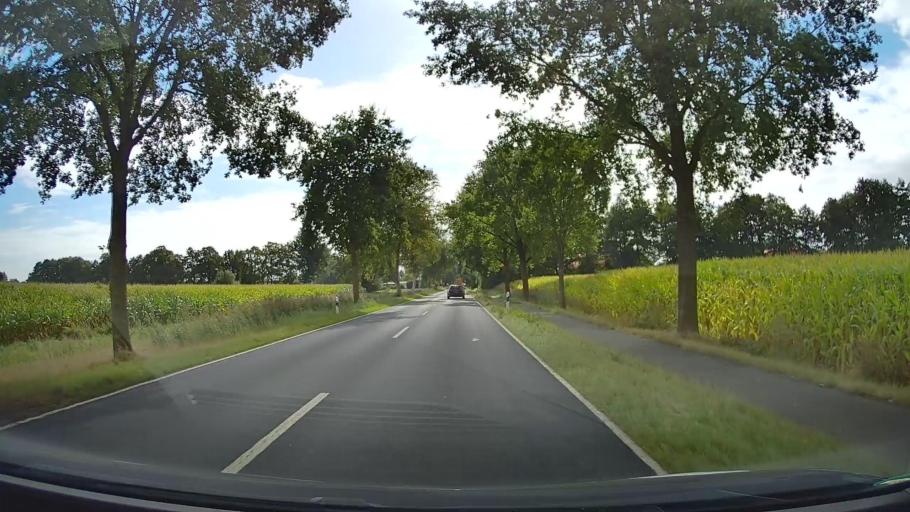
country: DE
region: Lower Saxony
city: Rhade
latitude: 53.3332
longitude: 9.1112
